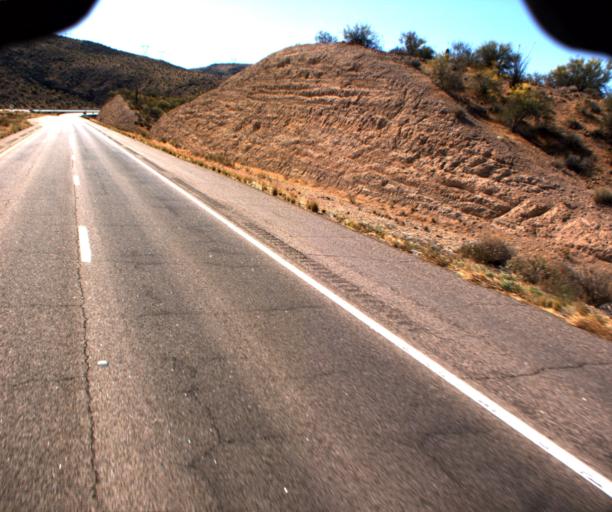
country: US
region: Arizona
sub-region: Yavapai County
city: Bagdad
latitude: 34.5816
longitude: -113.4971
